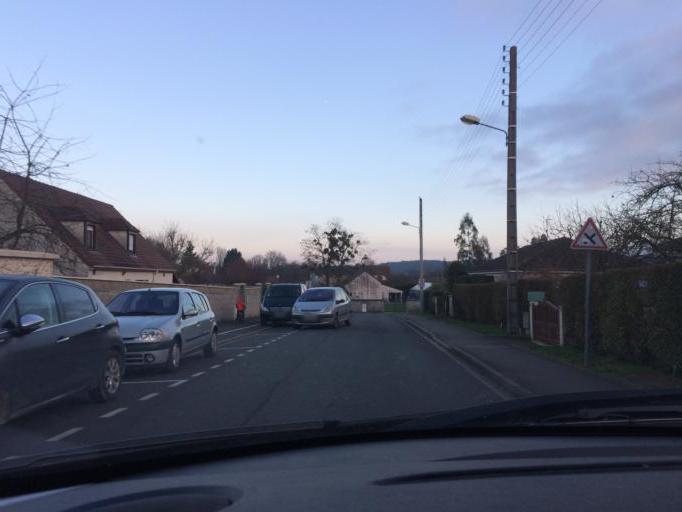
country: FR
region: Ile-de-France
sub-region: Departement de l'Essonne
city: Etrechy
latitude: 48.4899
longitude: 2.1865
